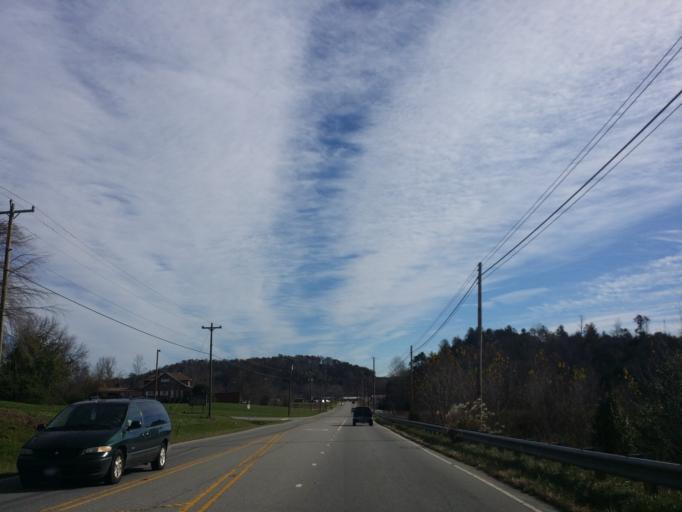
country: US
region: North Carolina
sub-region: McDowell County
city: West Marion
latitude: 35.6909
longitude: -82.0701
